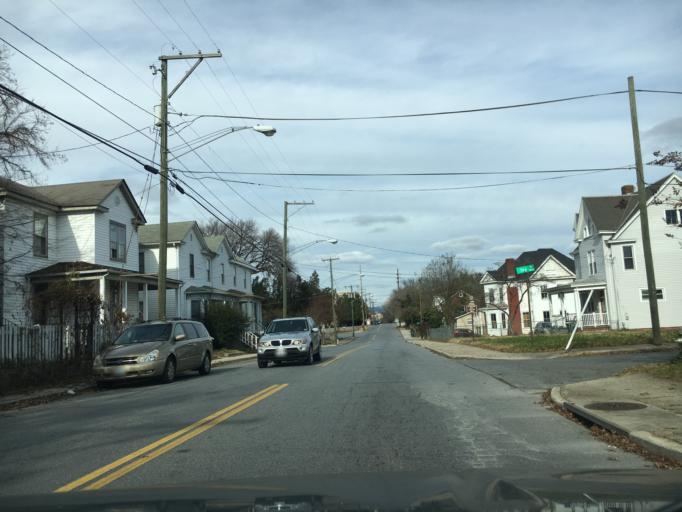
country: US
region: Virginia
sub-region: City of Lynchburg
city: Lynchburg
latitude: 37.4042
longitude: -79.1435
